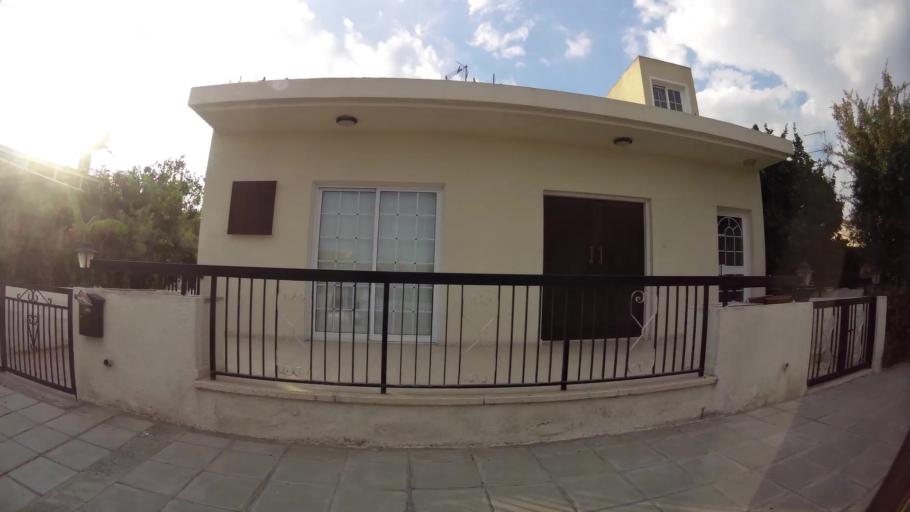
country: CY
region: Larnaka
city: Dhromolaxia
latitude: 34.8733
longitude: 33.5872
